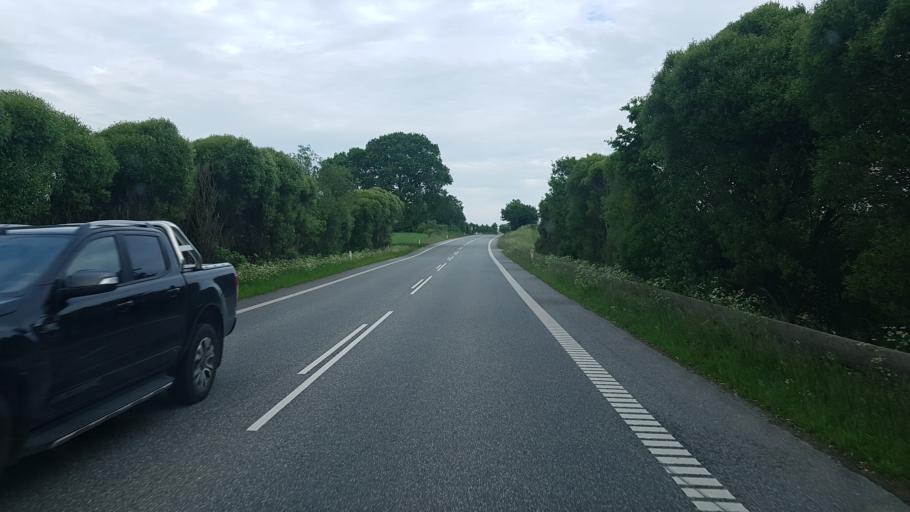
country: DK
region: South Denmark
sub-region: Vejen Kommune
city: Rodding
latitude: 55.3895
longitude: 9.0438
